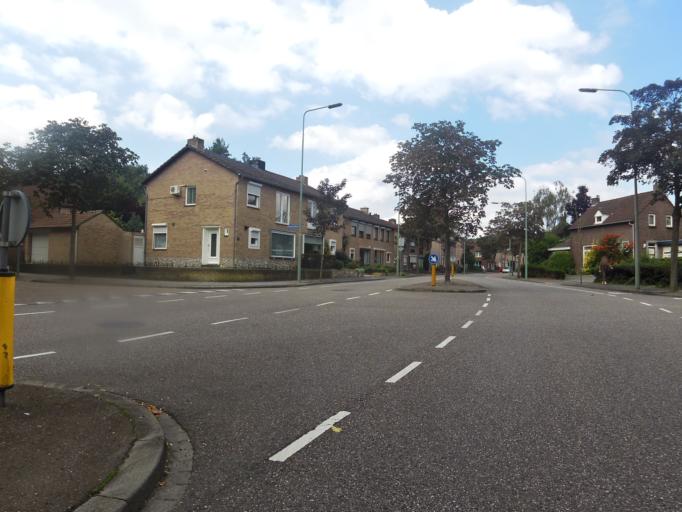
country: NL
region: Limburg
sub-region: Gemeente Heerlen
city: Hoensbroek
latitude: 50.9254
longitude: 5.9229
